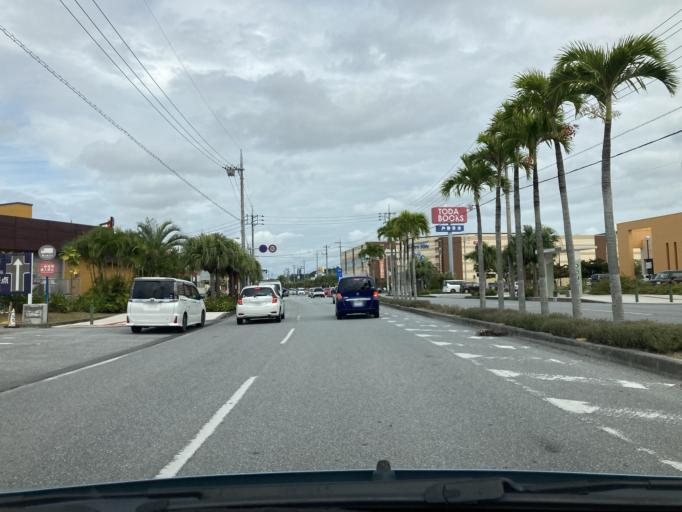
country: JP
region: Okinawa
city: Itoman
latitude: 26.1578
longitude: 127.6578
